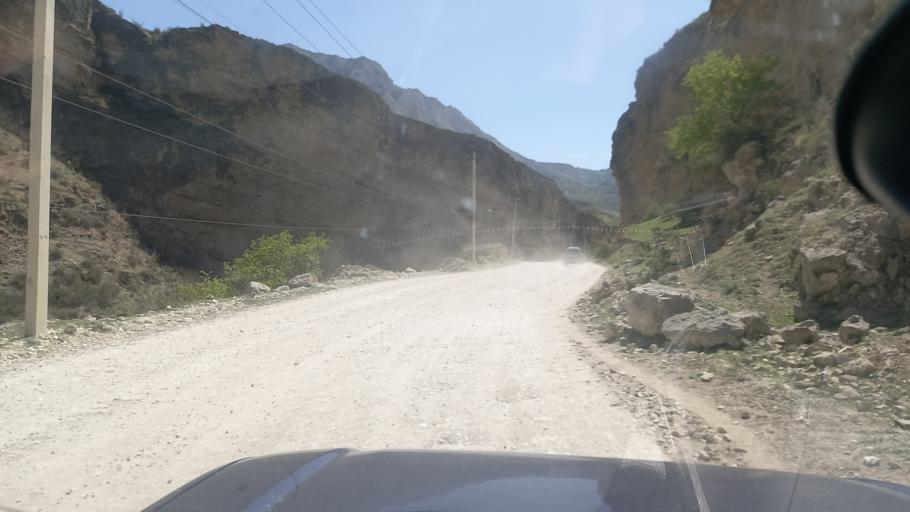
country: RU
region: Dagestan
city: Gunib
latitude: 42.4726
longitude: 46.8793
